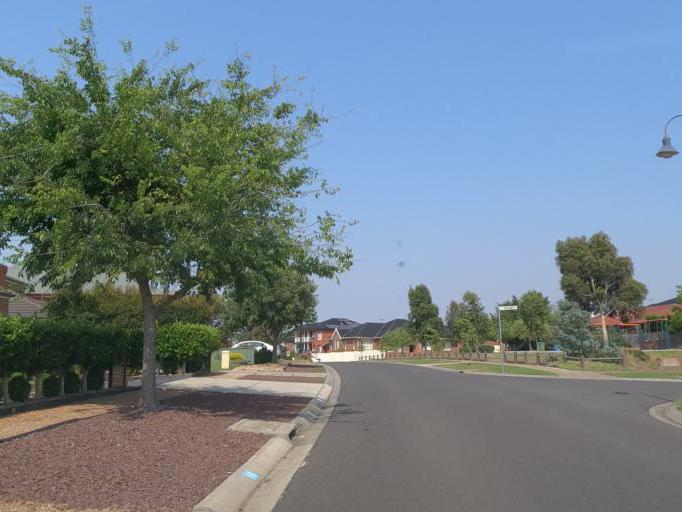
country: AU
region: Victoria
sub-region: Hume
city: Attwood
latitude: -37.6719
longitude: 144.8891
